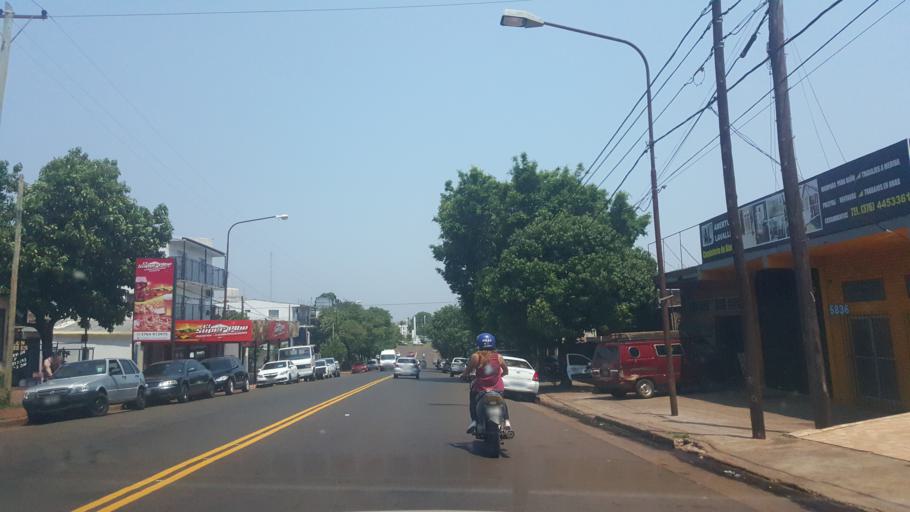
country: AR
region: Misiones
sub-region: Departamento de Capital
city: Posadas
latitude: -27.4004
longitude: -55.9098
